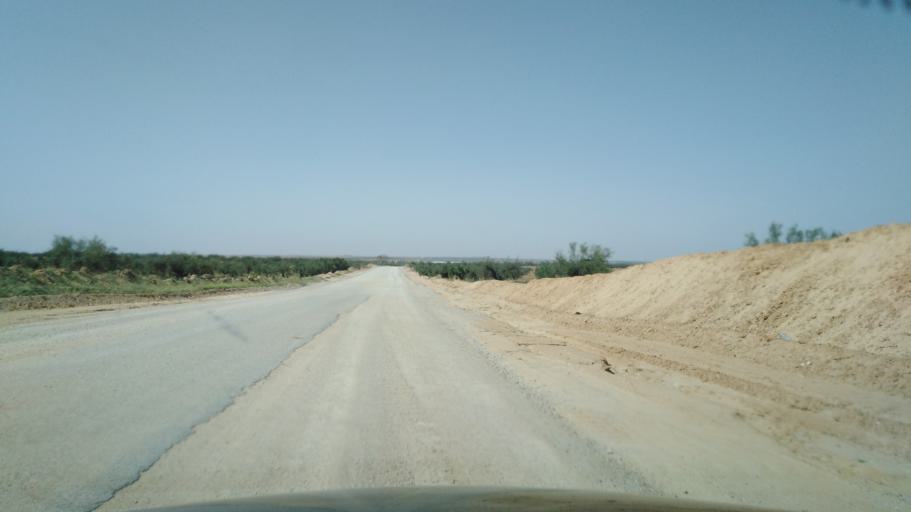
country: TN
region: Safaqis
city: Sfax
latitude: 34.7090
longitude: 10.4962
